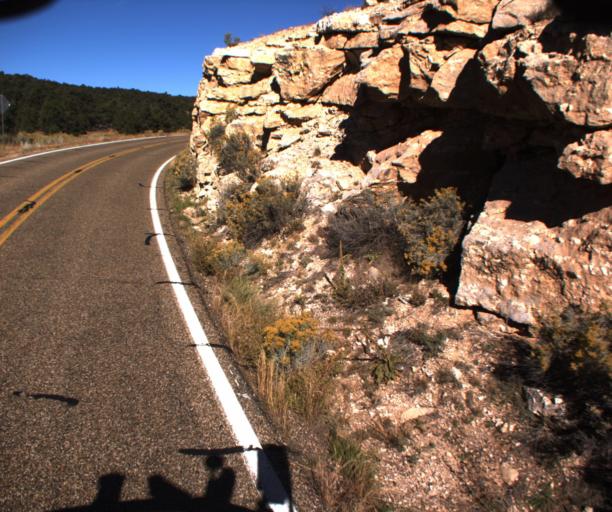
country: US
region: Arizona
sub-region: Coconino County
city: Fredonia
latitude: 36.7300
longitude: -112.0931
